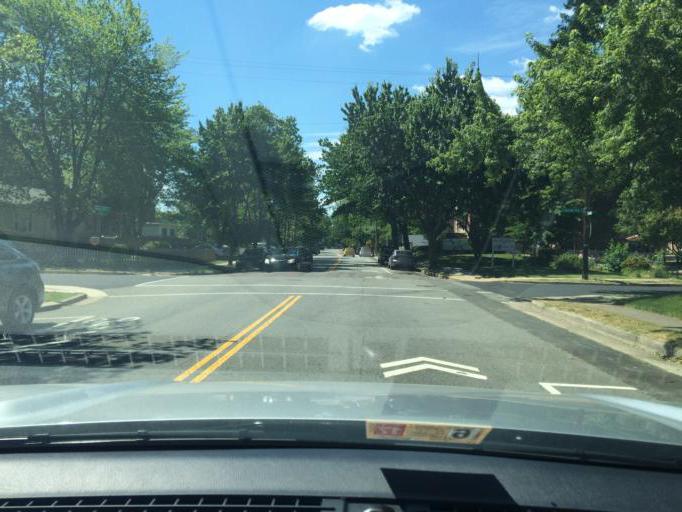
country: US
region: Virginia
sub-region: City of Alexandria
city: Alexandria
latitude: 38.8145
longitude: -77.0623
